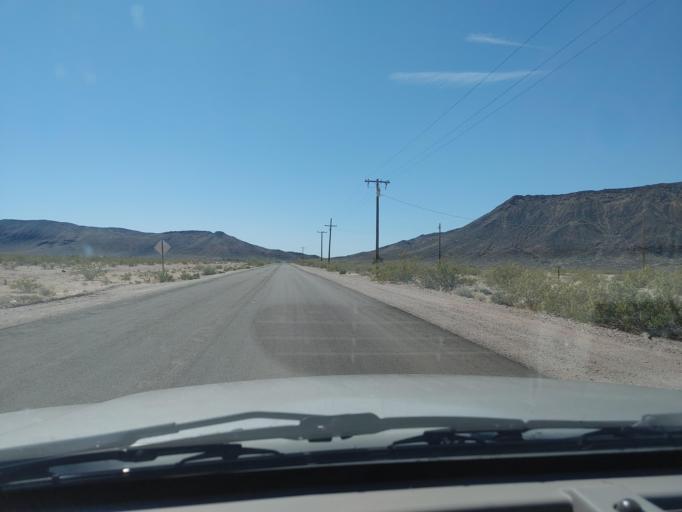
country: US
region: Arizona
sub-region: Maricopa County
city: Gila Bend
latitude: 33.0192
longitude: -113.3404
